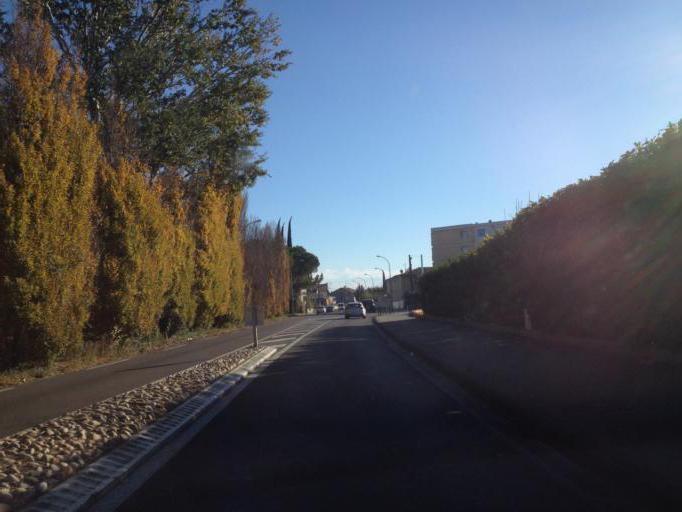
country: FR
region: Provence-Alpes-Cote d'Azur
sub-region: Departement du Vaucluse
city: Orange
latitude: 44.1427
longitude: 4.8129
